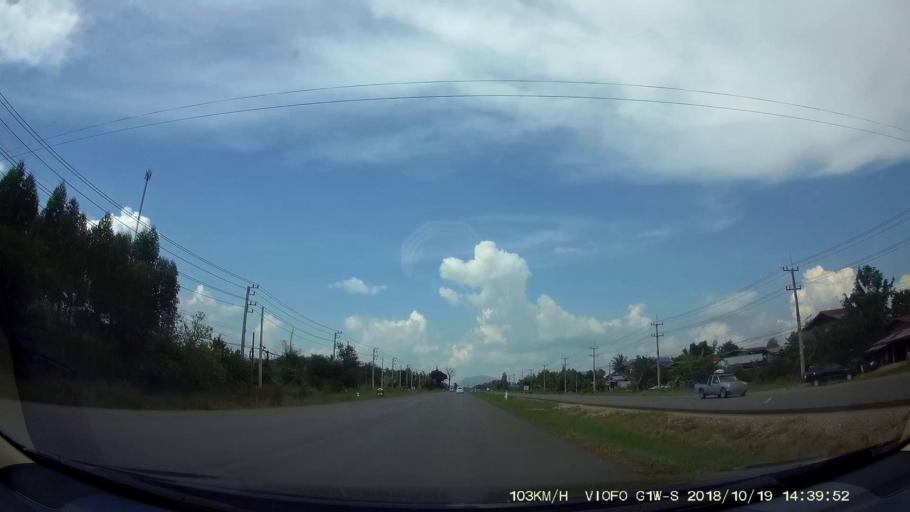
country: TH
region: Chaiyaphum
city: Kaeng Khro
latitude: 16.2322
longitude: 102.1949
